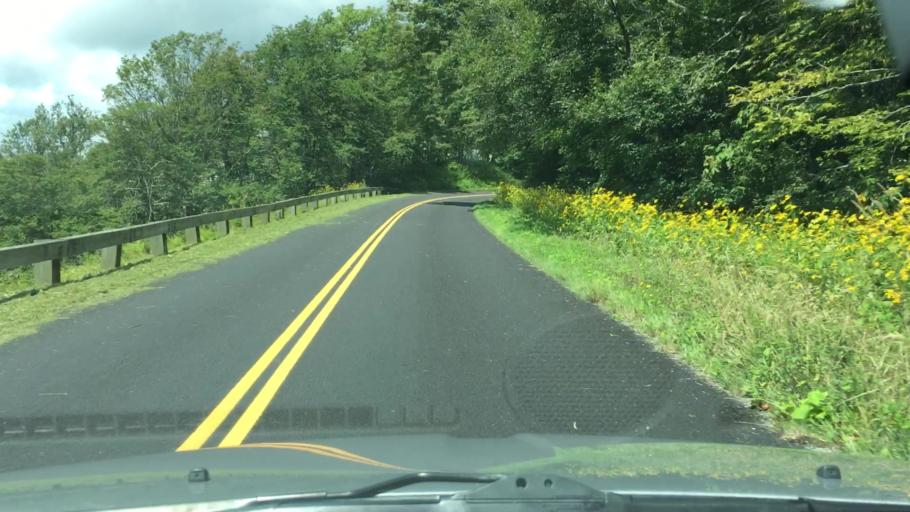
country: US
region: North Carolina
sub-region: Buncombe County
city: Black Mountain
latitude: 35.7403
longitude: -82.3406
